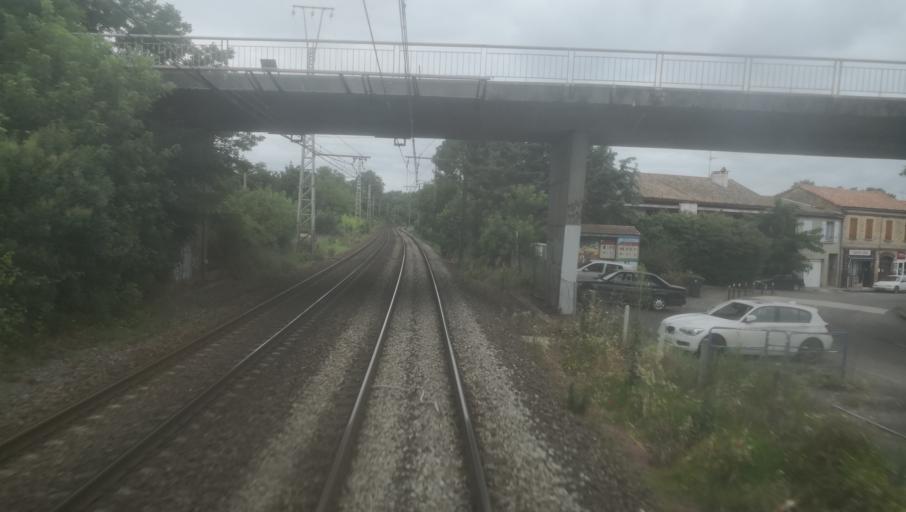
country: FR
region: Midi-Pyrenees
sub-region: Departement de la Haute-Garonne
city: Saint-Jory
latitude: 43.7403
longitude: 1.3697
